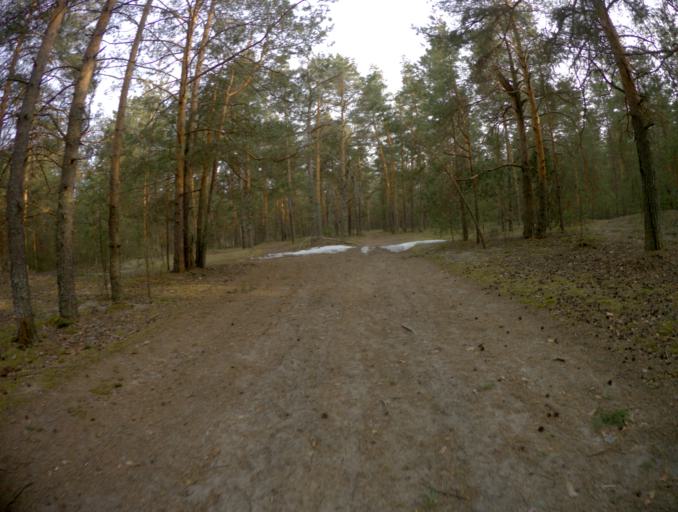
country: RU
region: Vladimir
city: Kommunar
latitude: 56.0823
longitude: 40.4370
